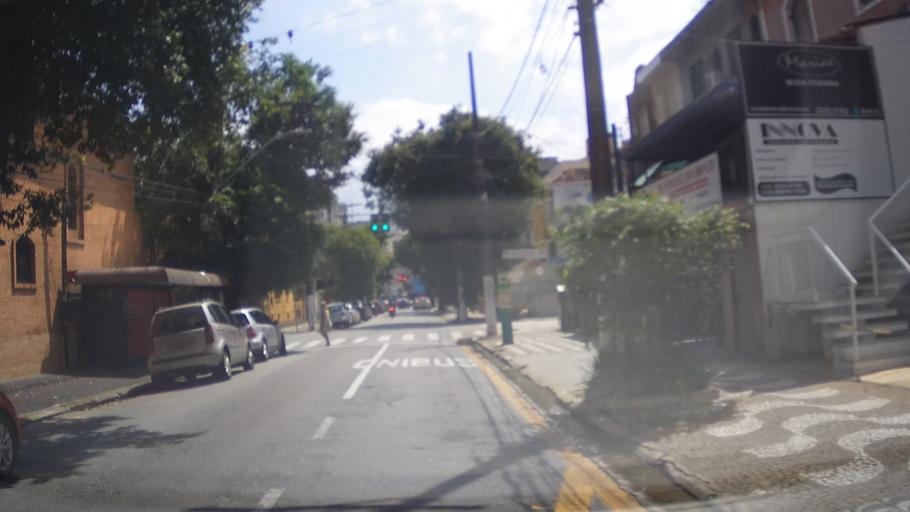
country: BR
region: Sao Paulo
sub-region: Santos
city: Santos
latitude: -23.9649
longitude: -46.3440
